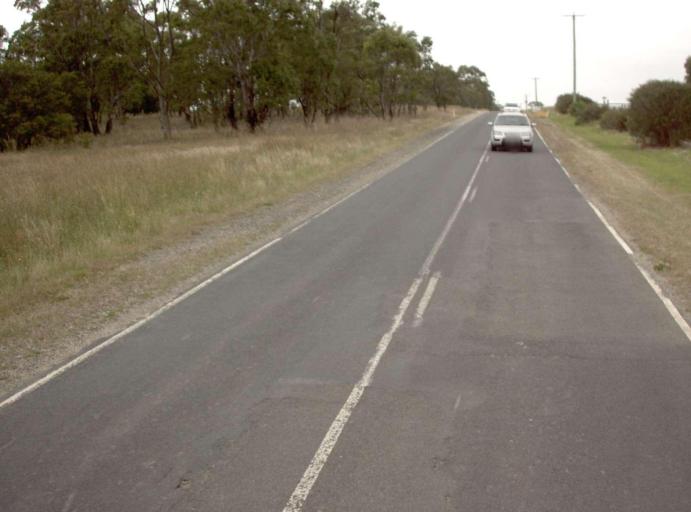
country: AU
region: Victoria
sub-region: Wellington
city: Heyfield
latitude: -38.0376
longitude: 146.7667
